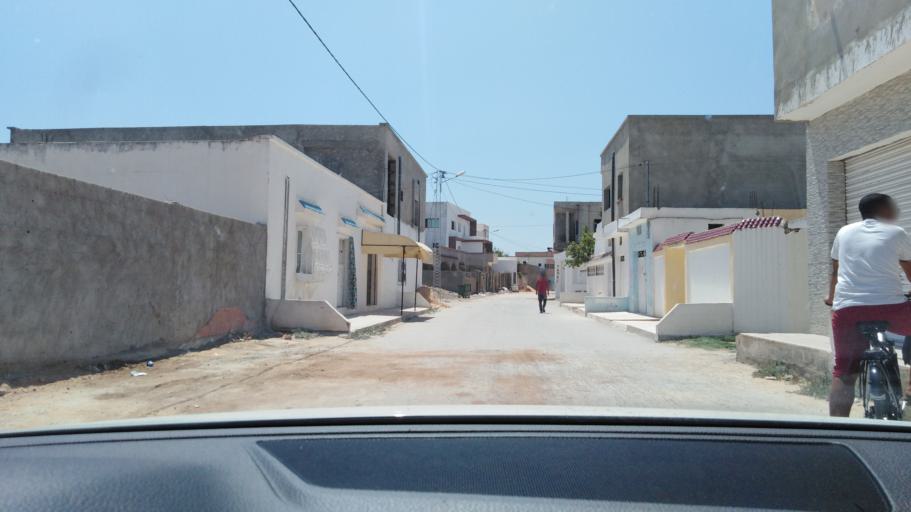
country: TN
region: Al Qayrawan
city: Sbikha
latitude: 36.1166
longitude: 10.0943
